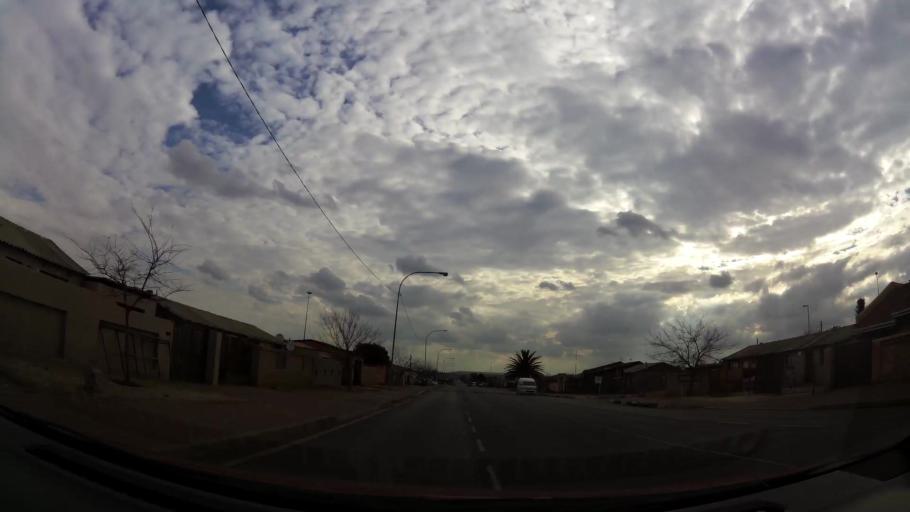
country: ZA
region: Gauteng
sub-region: City of Johannesburg Metropolitan Municipality
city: Soweto
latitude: -26.2488
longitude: 27.8262
